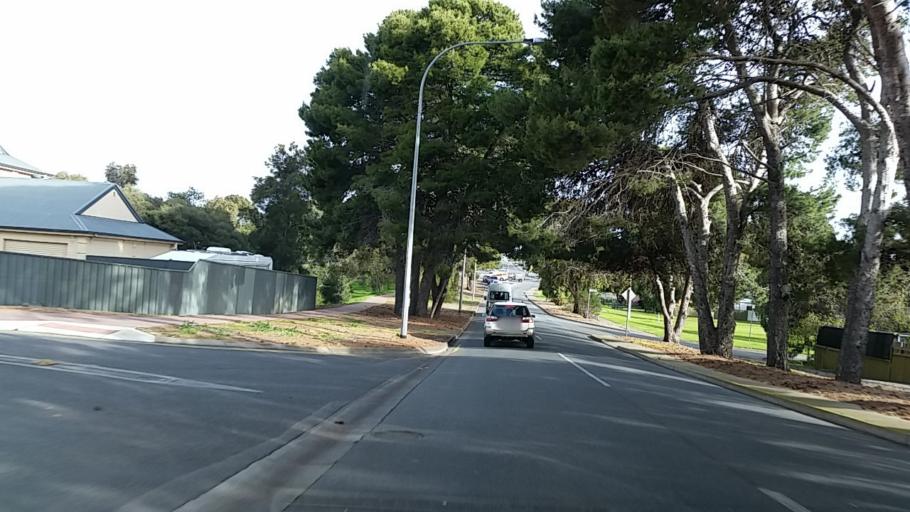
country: AU
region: South Australia
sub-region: Onkaparinga
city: Reynella
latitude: -35.1031
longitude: 138.5347
